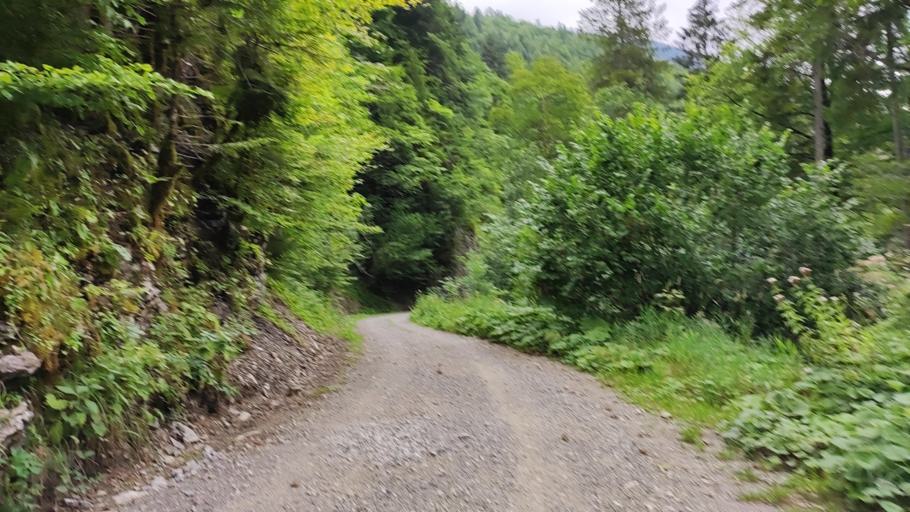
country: AT
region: Vorarlberg
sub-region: Politischer Bezirk Feldkirch
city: Feldkirch
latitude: 47.1953
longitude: 9.6046
